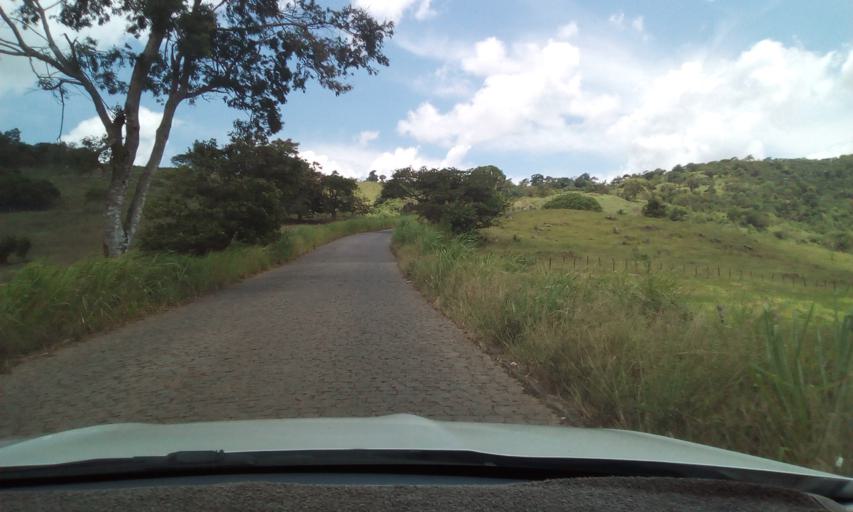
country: BR
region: Pernambuco
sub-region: Bonito
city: Bonito
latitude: -8.4874
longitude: -35.7312
